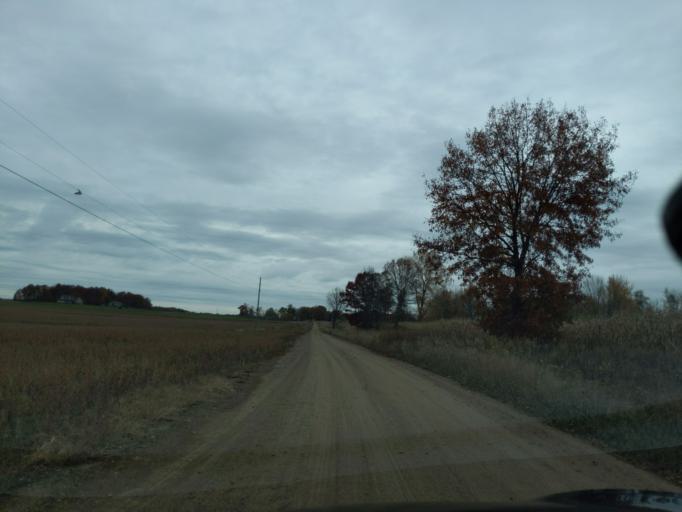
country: US
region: Michigan
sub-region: Eaton County
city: Eaton Rapids
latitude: 42.4222
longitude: -84.6004
